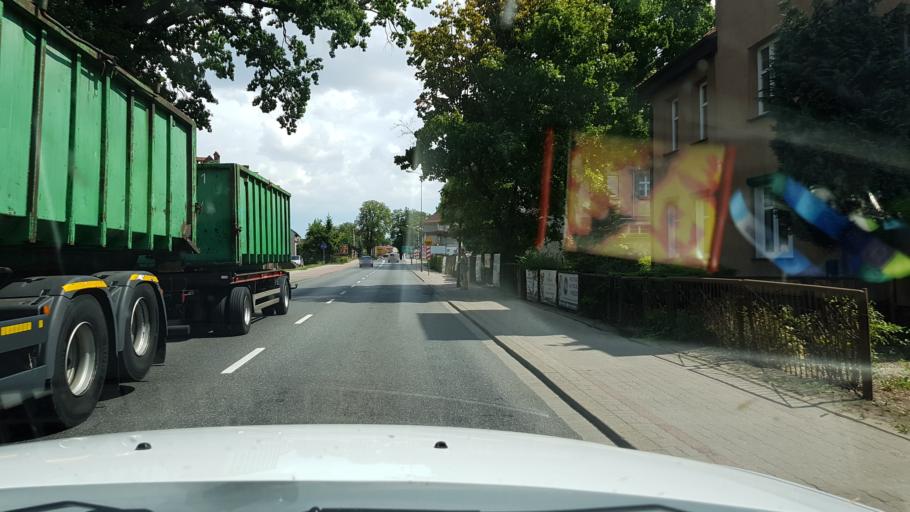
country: PL
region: West Pomeranian Voivodeship
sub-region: Powiat walecki
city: Walcz
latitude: 53.2786
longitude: 16.4597
